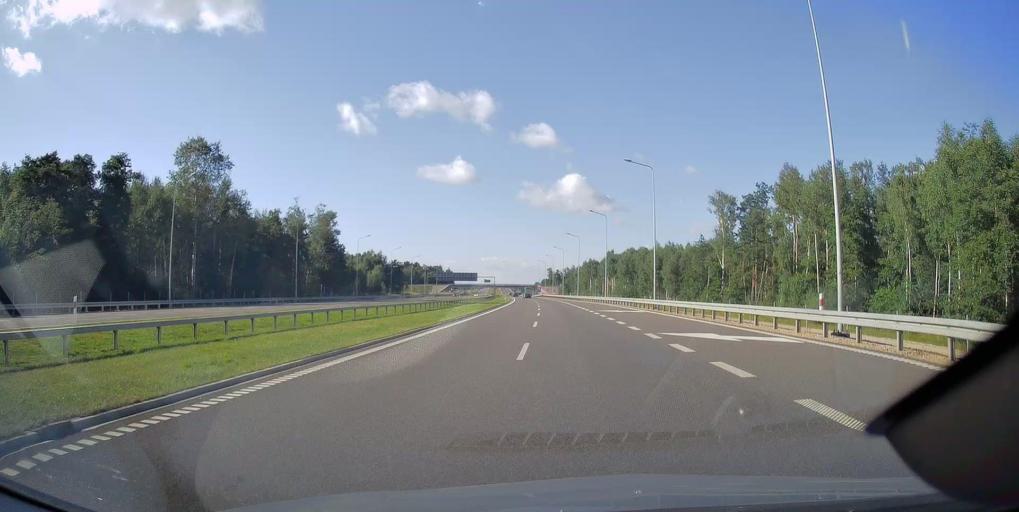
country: PL
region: Masovian Voivodeship
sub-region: Powiat szydlowiecki
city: Oronsko
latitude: 51.3433
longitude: 21.0157
